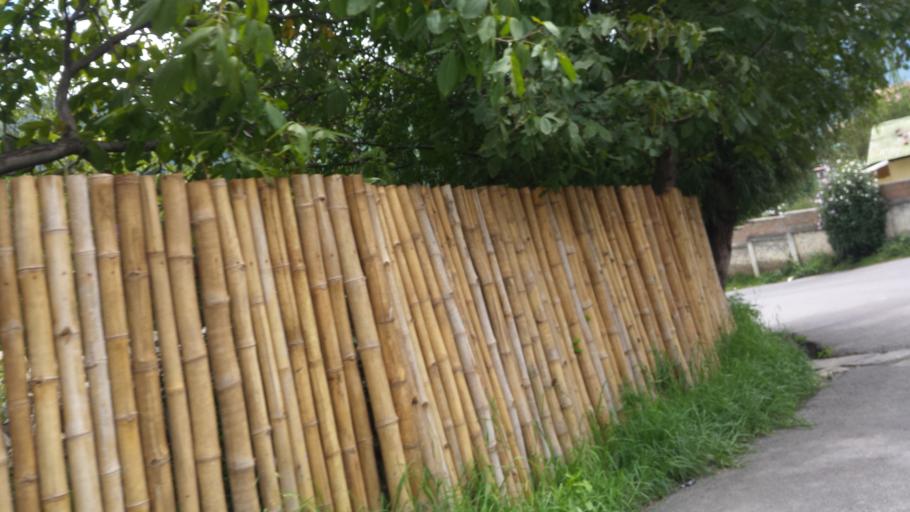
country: BT
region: Thimphu
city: Thimphu
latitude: 27.4732
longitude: 89.6306
